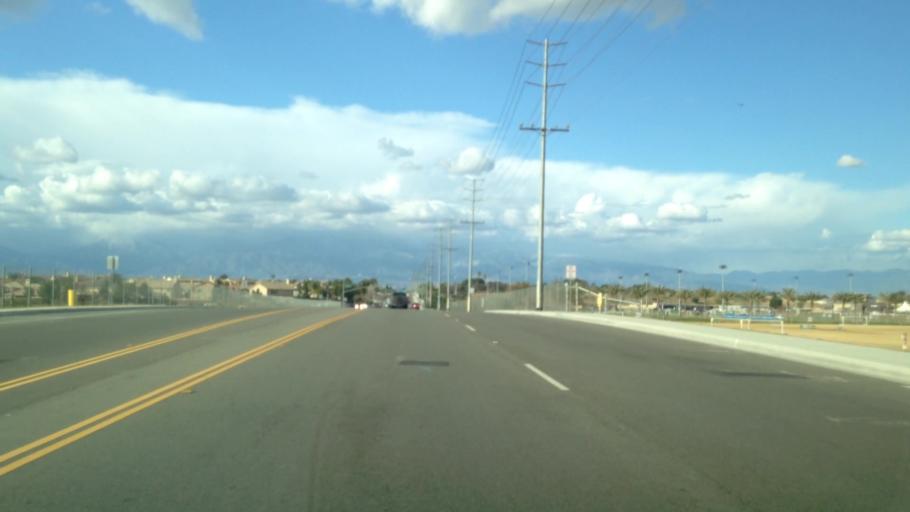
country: US
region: California
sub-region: Riverside County
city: Norco
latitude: 33.9489
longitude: -117.5583
